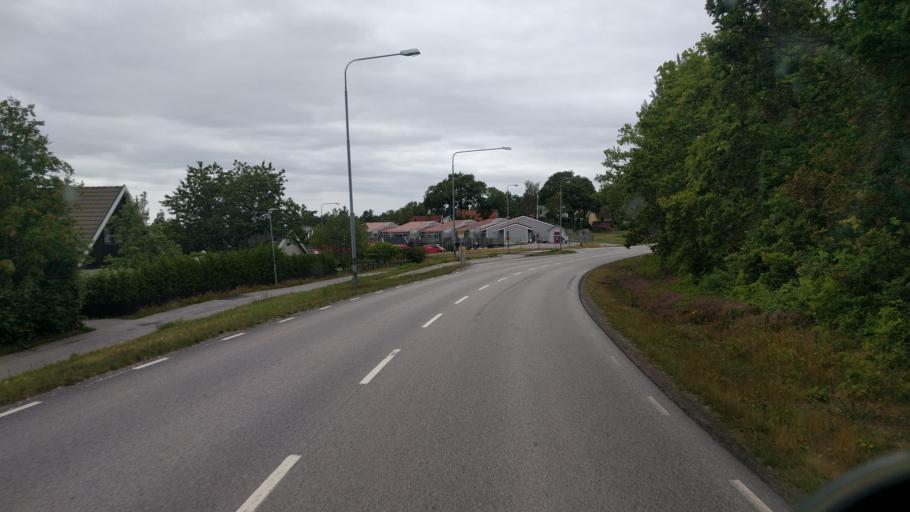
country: SE
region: Kalmar
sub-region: Vasterviks Kommun
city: Vaestervik
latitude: 57.7538
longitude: 16.6087
